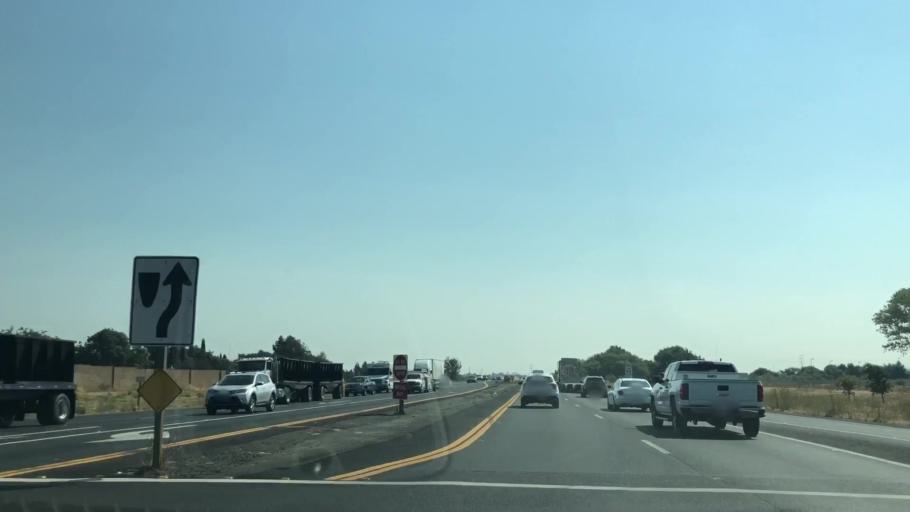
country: US
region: California
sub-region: Solano County
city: Suisun
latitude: 38.2403
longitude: -122.0662
